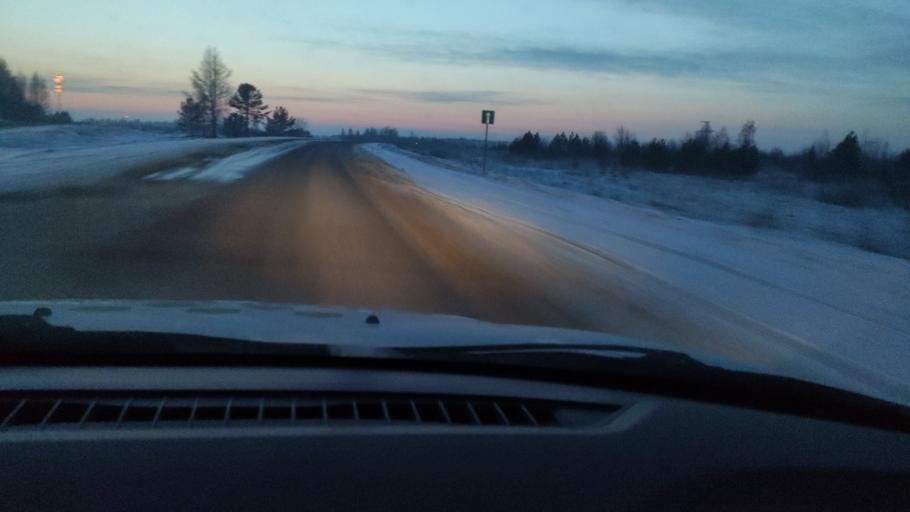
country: RU
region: Perm
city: Kungur
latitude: 57.4064
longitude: 56.8964
